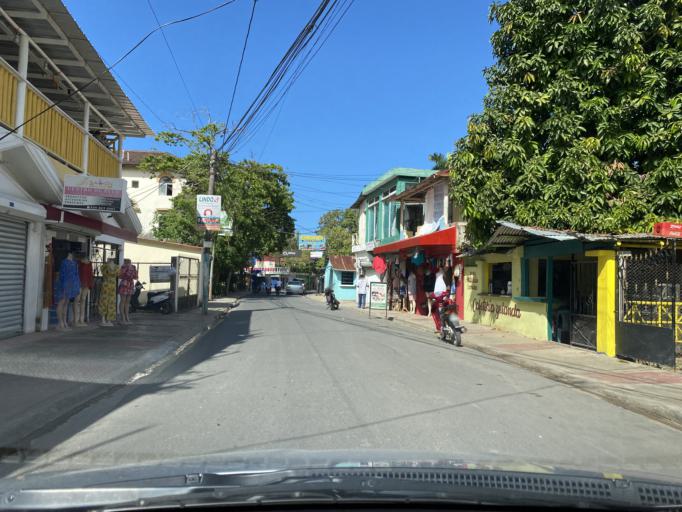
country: DO
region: Samana
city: Las Terrenas
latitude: 19.3144
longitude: -69.5414
